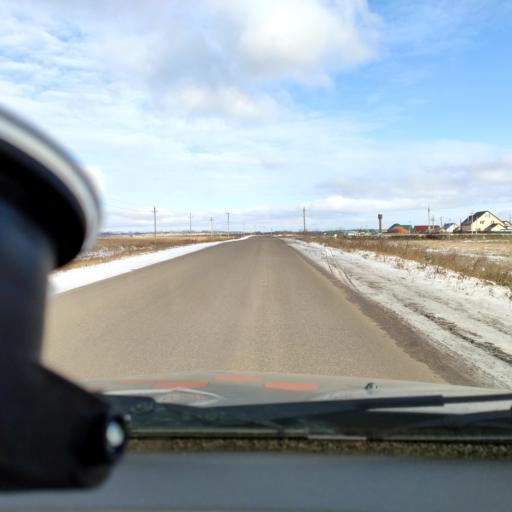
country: RU
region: Bashkortostan
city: Mikhaylovka
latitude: 54.8087
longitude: 55.7831
